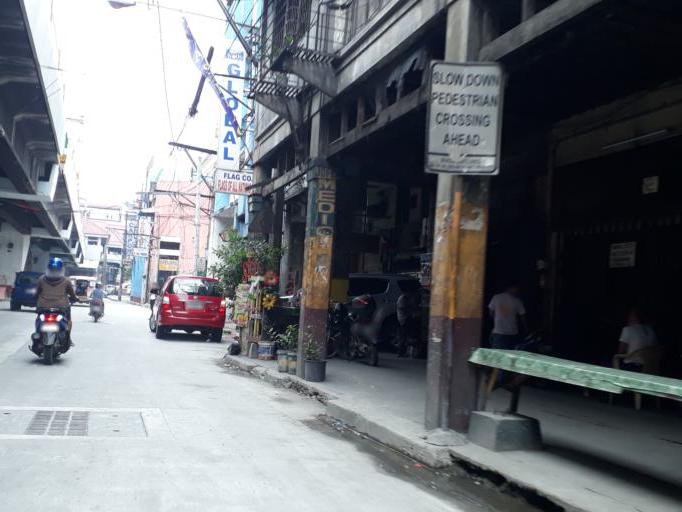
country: PH
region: Metro Manila
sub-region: City of Manila
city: Manila
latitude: 14.6071
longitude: 120.9822
